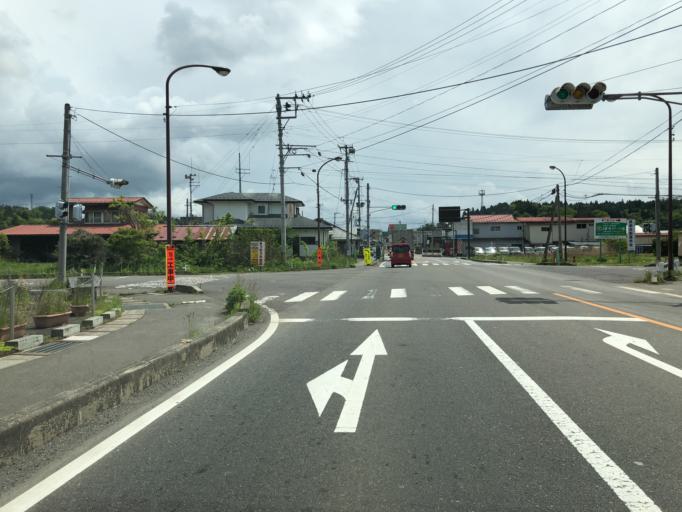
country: JP
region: Fukushima
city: Ishikawa
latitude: 37.1033
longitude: 140.3484
